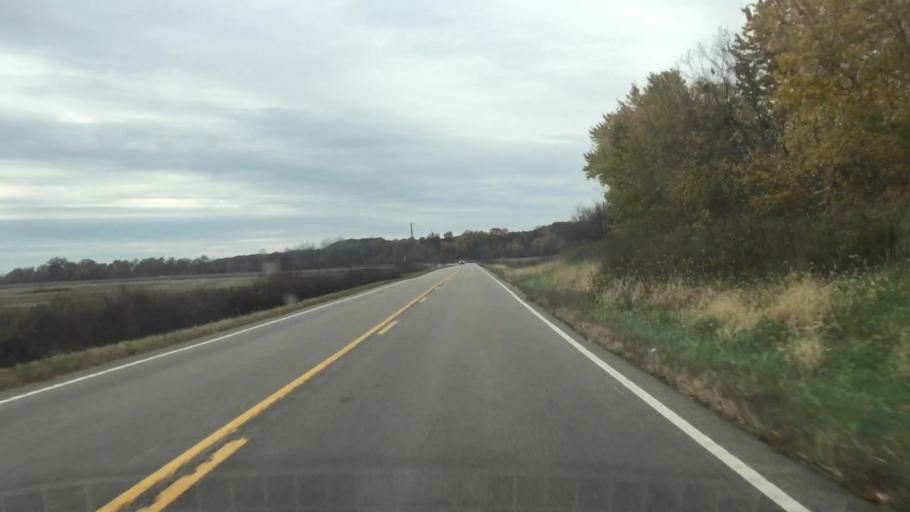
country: US
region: Missouri
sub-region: Callaway County
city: Fulton
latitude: 38.7076
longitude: -91.7484
